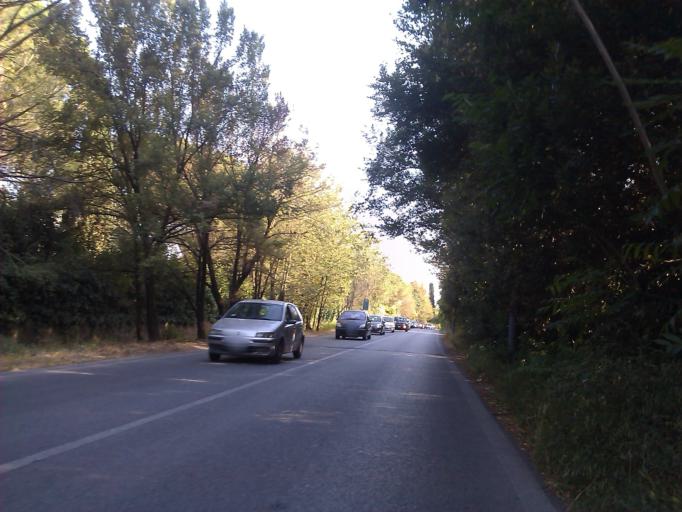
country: IT
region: Latium
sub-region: Citta metropolitana di Roma Capitale
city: Rome
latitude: 41.8366
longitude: 12.5414
